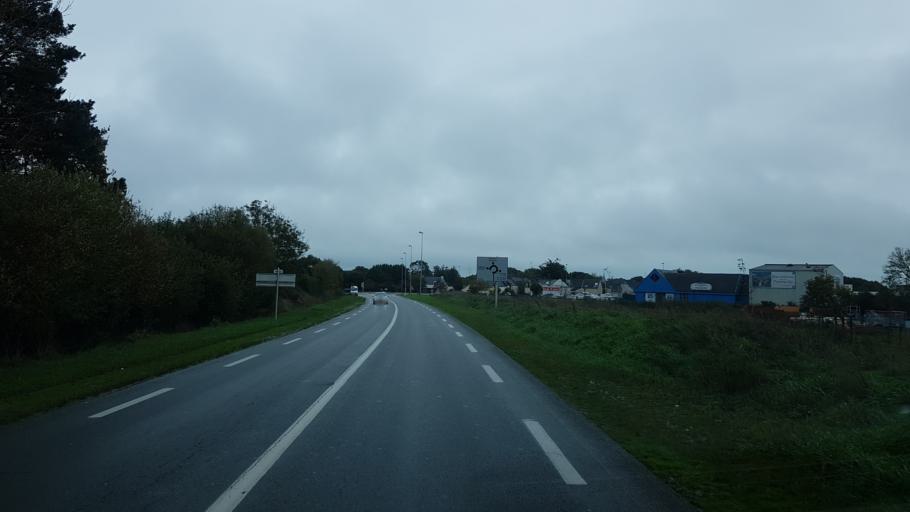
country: FR
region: Brittany
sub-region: Departement du Morbihan
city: Sarzeau
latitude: 47.5220
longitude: -2.7816
